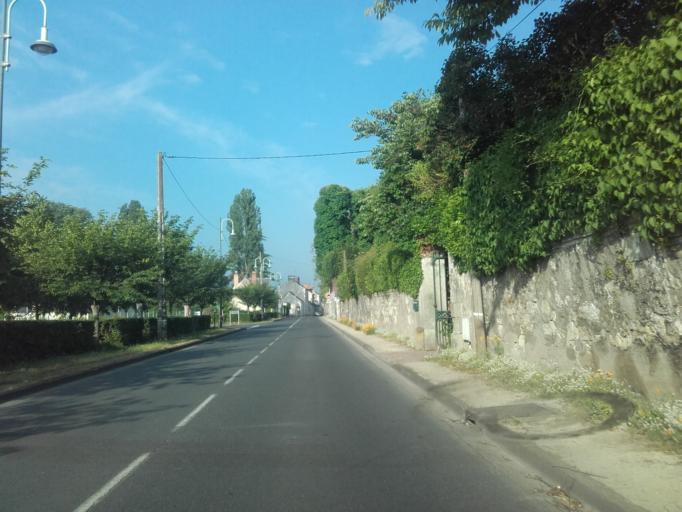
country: FR
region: Centre
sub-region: Departement d'Indre-et-Loire
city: Cinq-Mars-la-Pile
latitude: 47.3491
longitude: 0.4665
